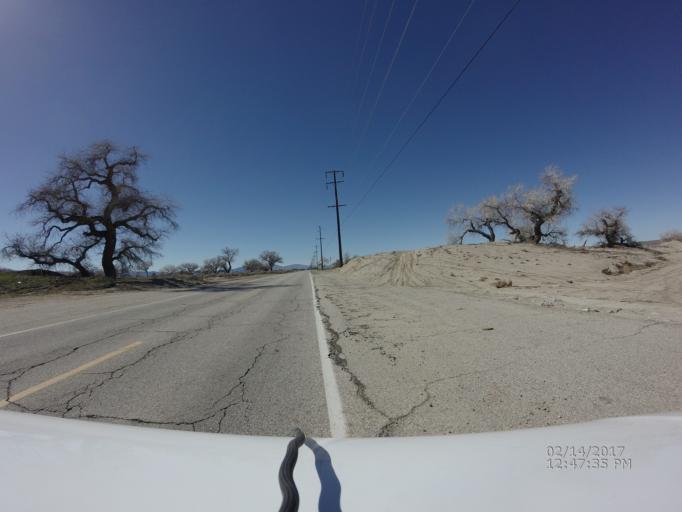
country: US
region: California
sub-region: Los Angeles County
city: Lake Los Angeles
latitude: 34.5800
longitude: -117.8715
